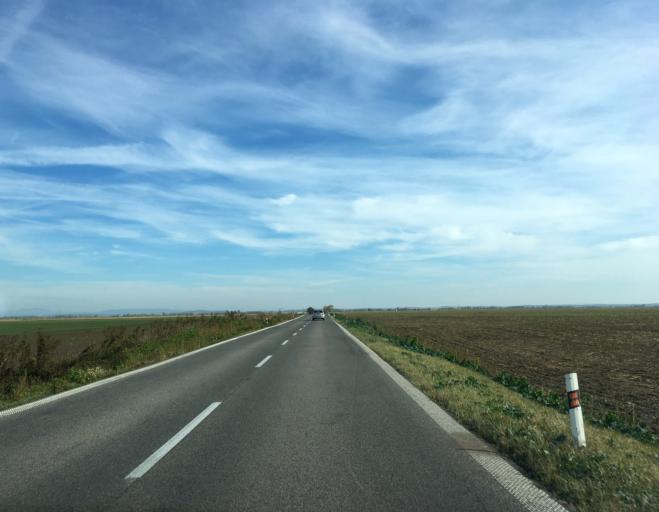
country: SK
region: Nitriansky
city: Zeliezovce
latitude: 48.0974
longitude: 18.5930
